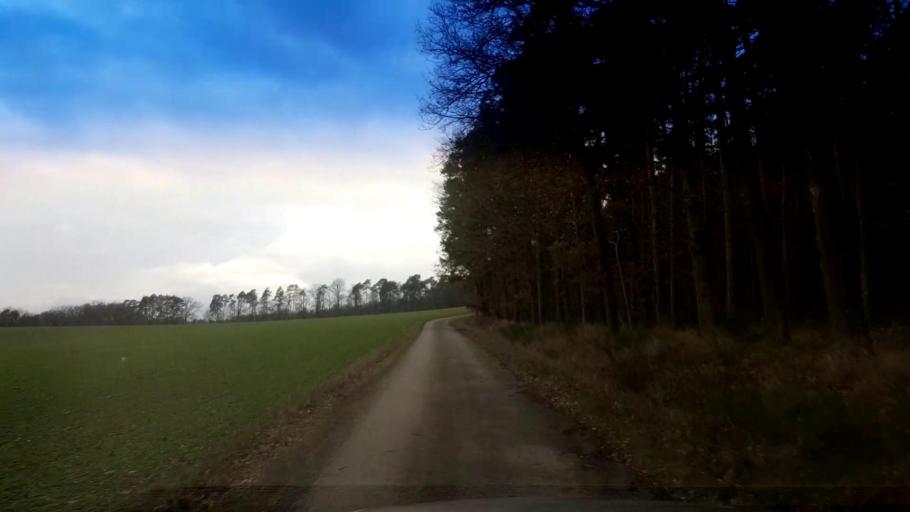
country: DE
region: Bavaria
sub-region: Upper Franconia
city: Lauter
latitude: 49.9554
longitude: 10.7659
